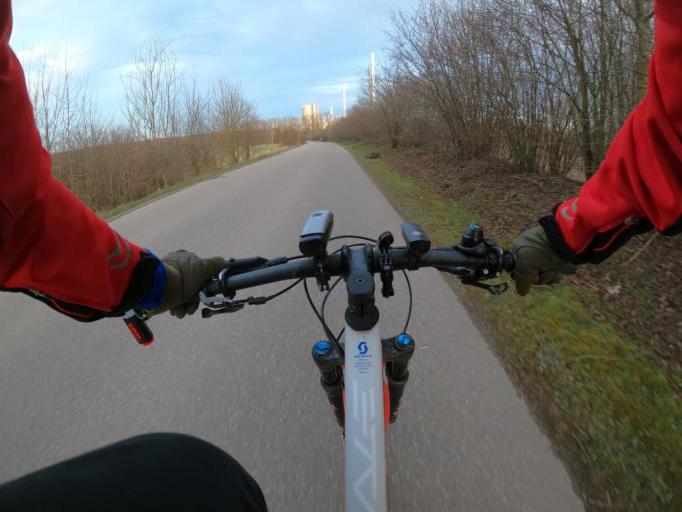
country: DE
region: Baden-Wuerttemberg
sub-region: Regierungsbezirk Stuttgart
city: Altbach
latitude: 48.7186
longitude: 9.3556
